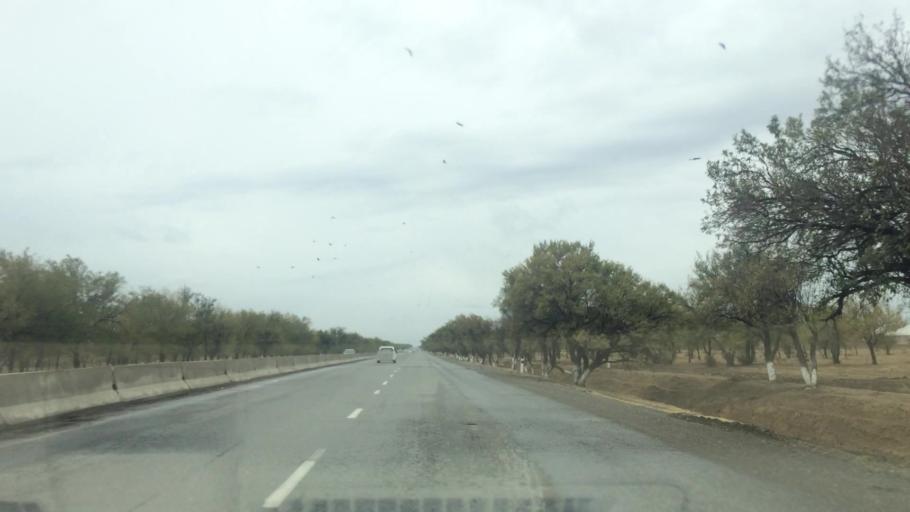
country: UZ
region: Samarqand
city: Bulung'ur
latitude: 39.8305
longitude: 67.4120
